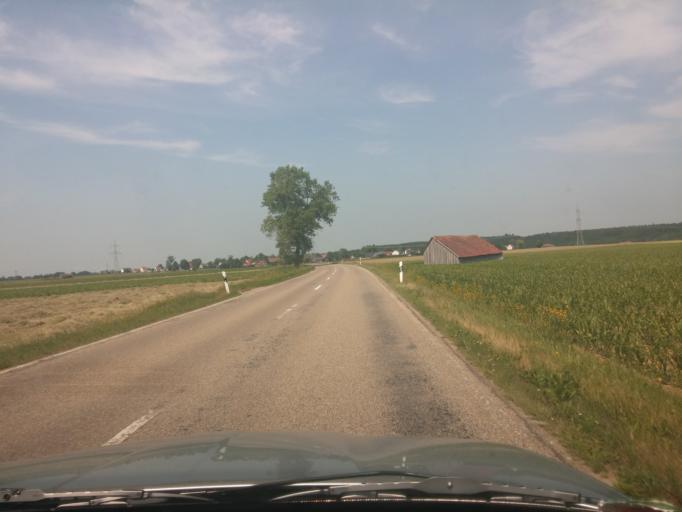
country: DE
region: Bavaria
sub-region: Swabia
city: Kronburg
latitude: 47.9414
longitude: 10.1627
